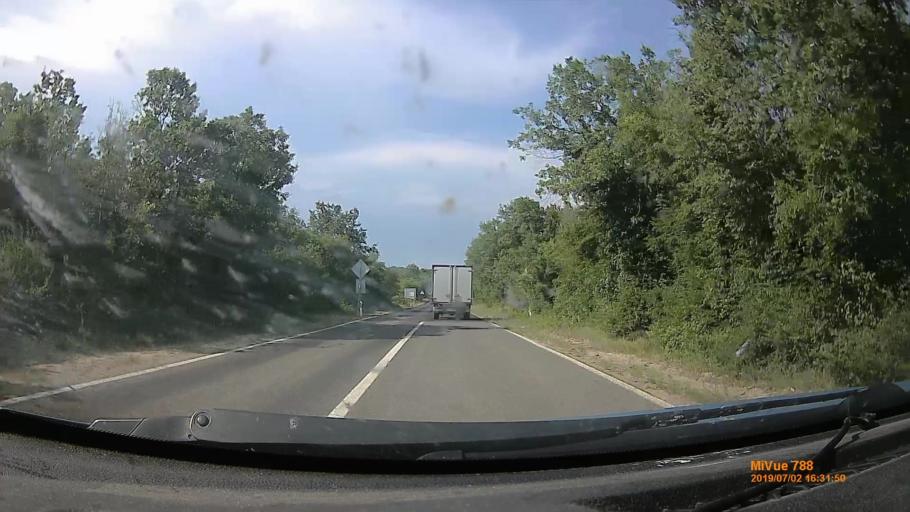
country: HR
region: Primorsko-Goranska
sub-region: Grad Krk
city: Krk
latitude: 45.0578
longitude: 14.4875
